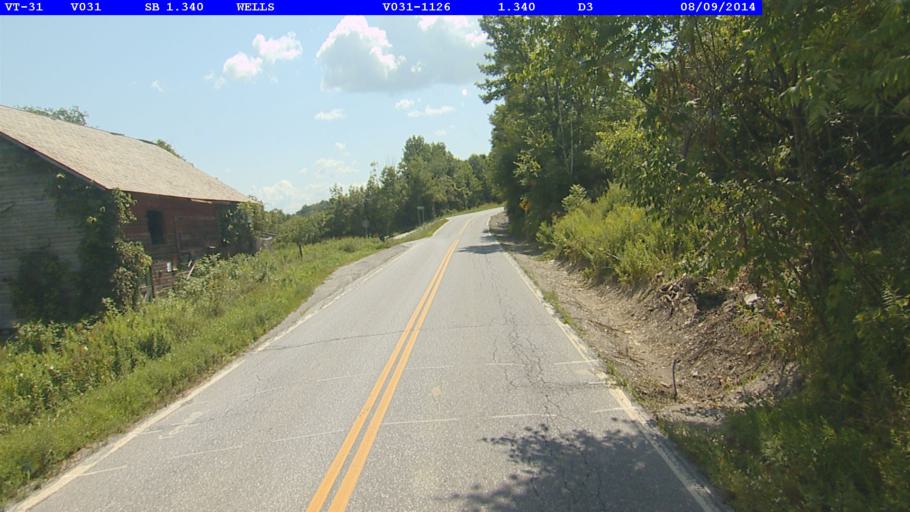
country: US
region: New York
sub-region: Washington County
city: Granville
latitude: 43.4563
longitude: -73.2416
